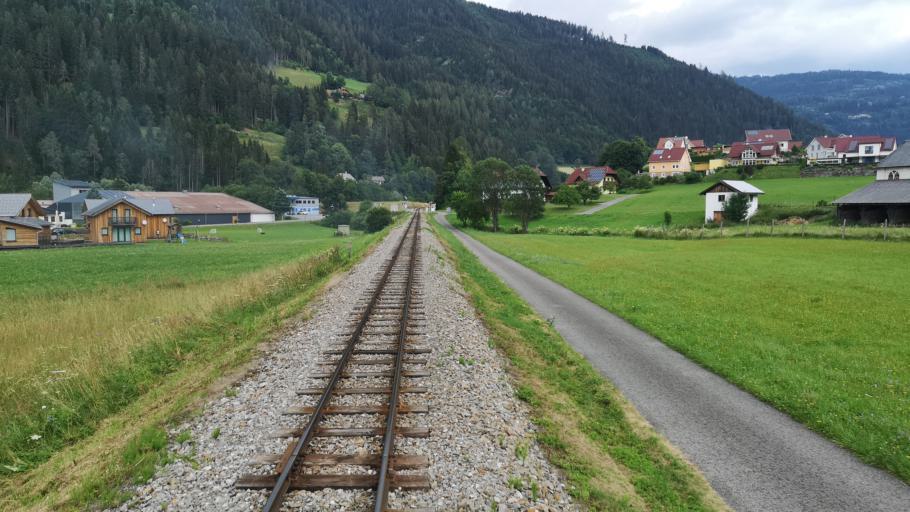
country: AT
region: Styria
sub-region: Politischer Bezirk Murau
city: Murau
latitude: 47.1099
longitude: 14.1464
